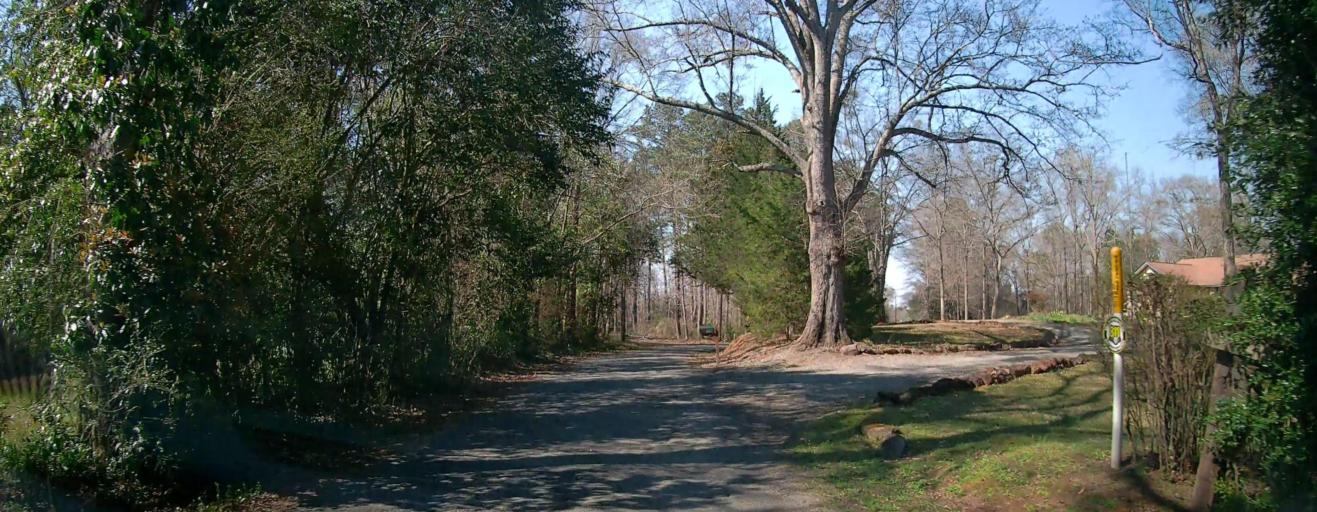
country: US
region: Georgia
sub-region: Jones County
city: Gray
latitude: 33.0019
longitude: -83.5593
